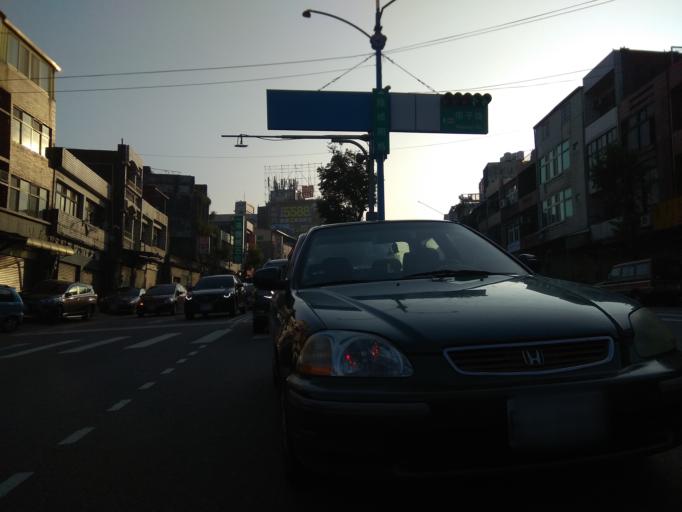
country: TW
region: Taiwan
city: Daxi
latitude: 24.9235
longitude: 121.1876
